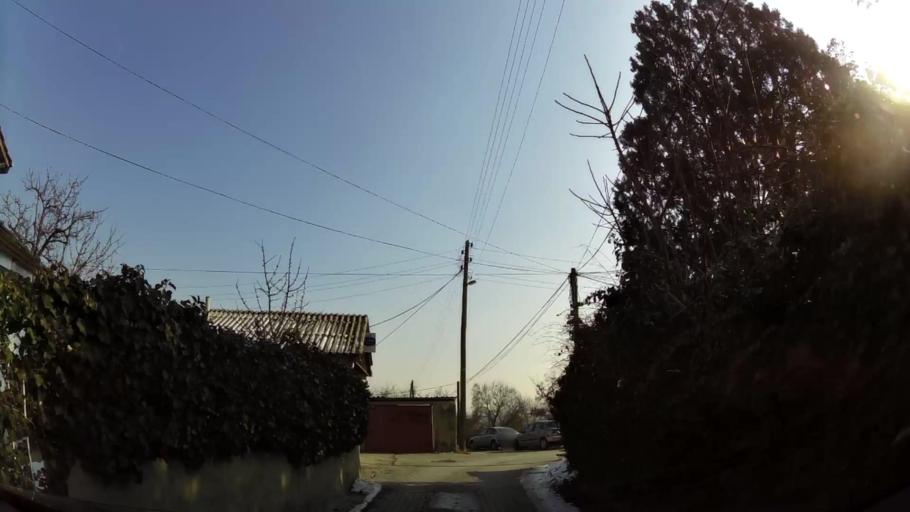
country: MK
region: Sopiste
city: Sopishte
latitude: 41.9747
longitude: 21.4362
